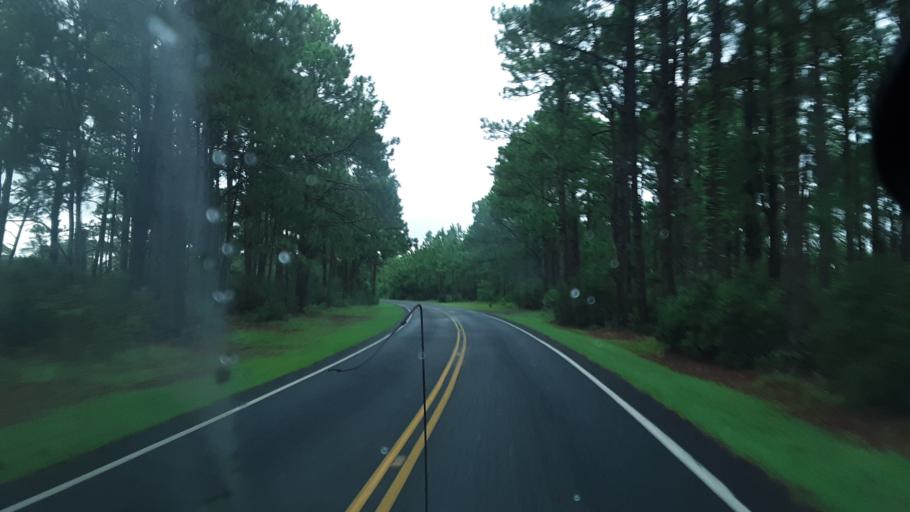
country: US
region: North Carolina
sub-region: Dare County
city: Wanchese
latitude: 35.8218
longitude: -75.5653
